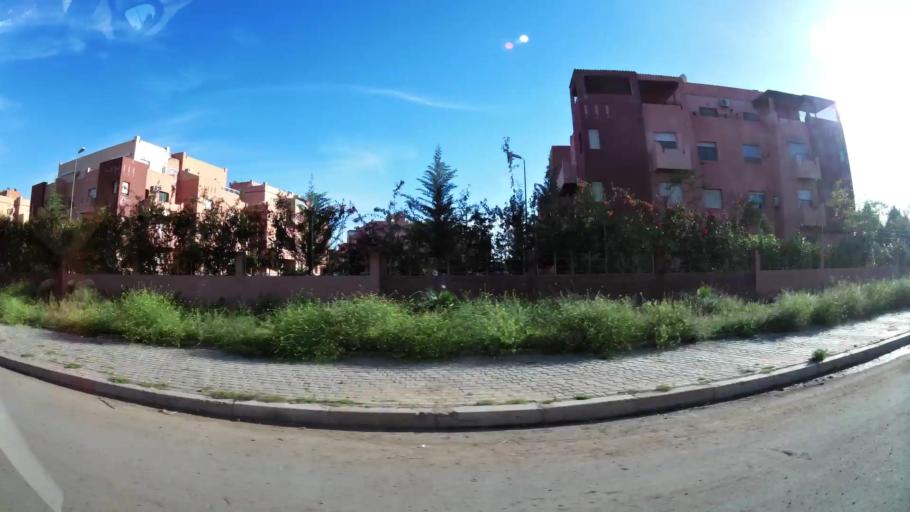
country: MA
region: Marrakech-Tensift-Al Haouz
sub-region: Marrakech
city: Marrakesh
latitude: 31.6786
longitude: -8.0650
